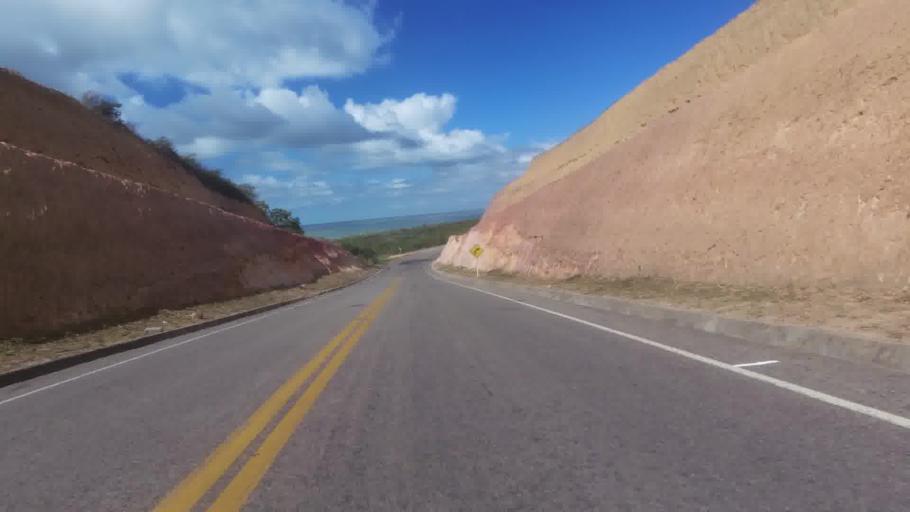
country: BR
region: Espirito Santo
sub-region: Marataizes
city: Marataizes
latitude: -21.1723
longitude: -40.9178
